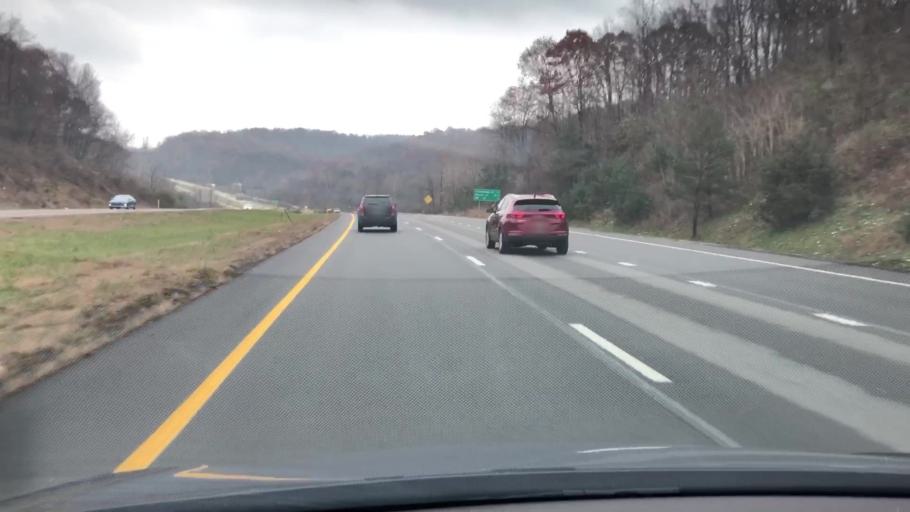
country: US
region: Pennsylvania
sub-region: Westmoreland County
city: New Stanton
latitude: 40.2156
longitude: -79.5916
